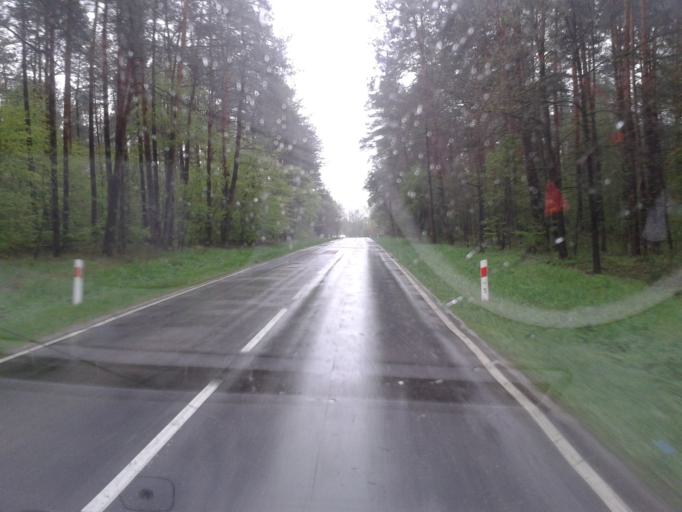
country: PL
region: Subcarpathian Voivodeship
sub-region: Powiat lubaczowski
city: Cieszanow
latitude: 50.2693
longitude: 23.1483
